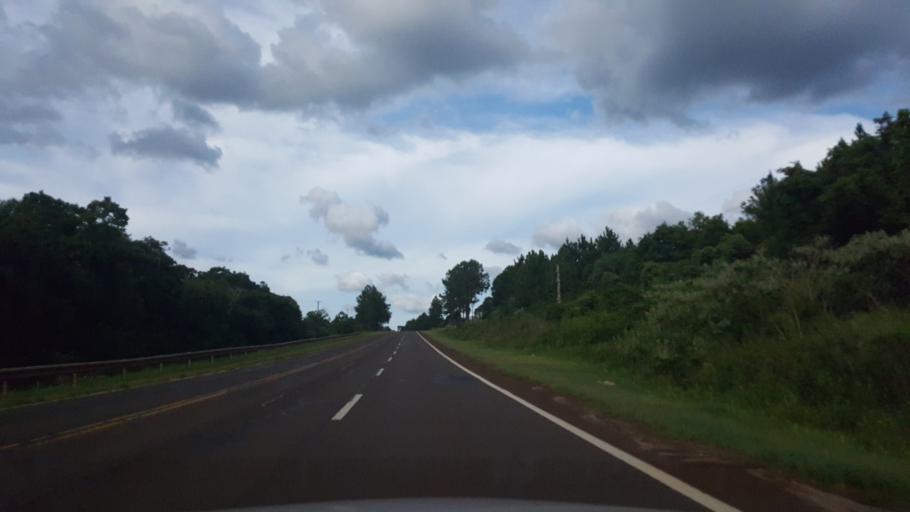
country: AR
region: Misiones
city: Gobernador Roca
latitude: -27.2194
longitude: -55.5005
